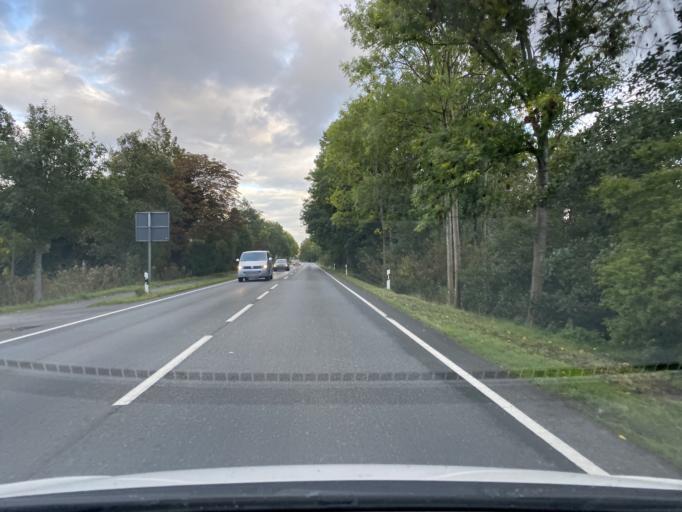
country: DE
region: Lower Saxony
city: Nordleda
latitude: 53.7993
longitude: 8.8577
